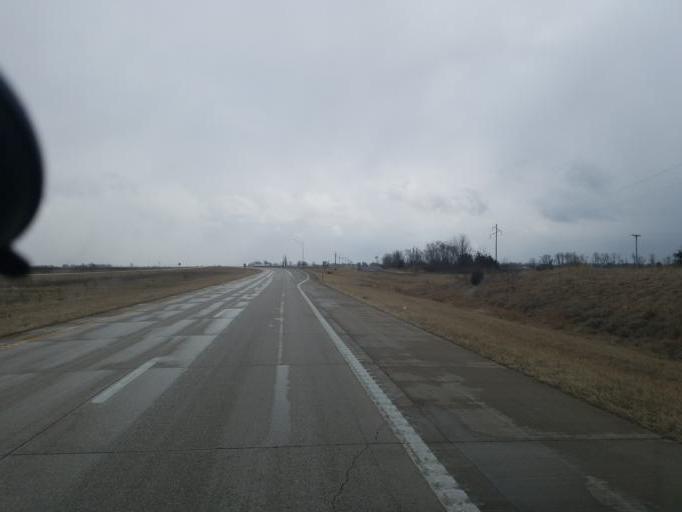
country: US
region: Missouri
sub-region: Randolph County
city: Moberly
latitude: 39.5344
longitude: -92.4467
